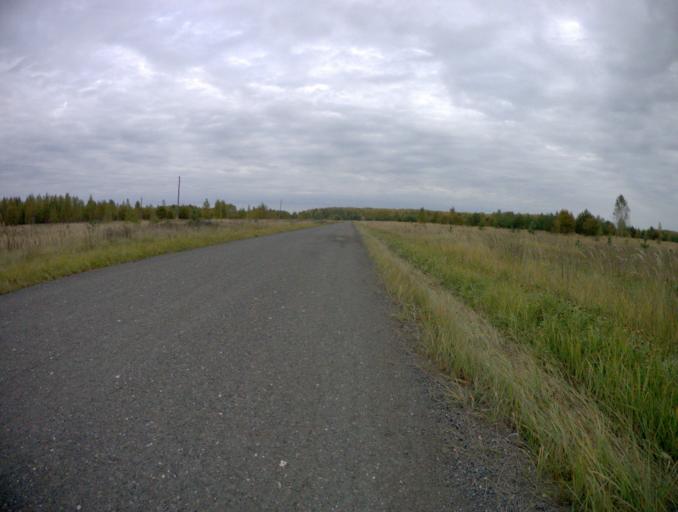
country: RU
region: Vladimir
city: Mstera
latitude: 56.3701
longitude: 41.8077
